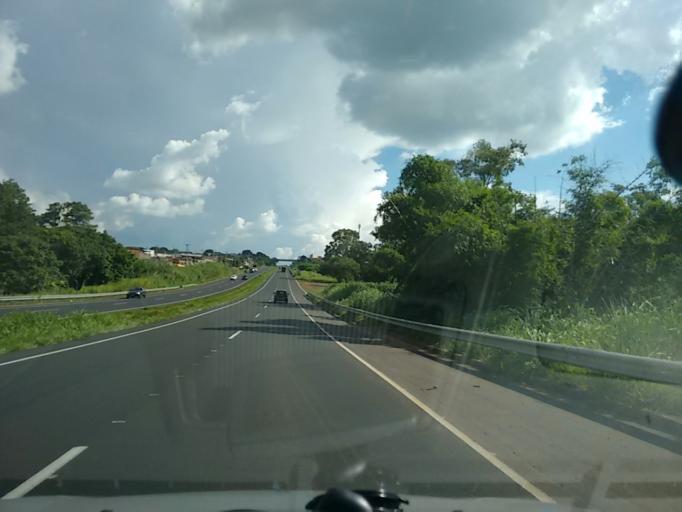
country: BR
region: Sao Paulo
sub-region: Marilia
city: Marilia
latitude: -22.2163
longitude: -49.9649
